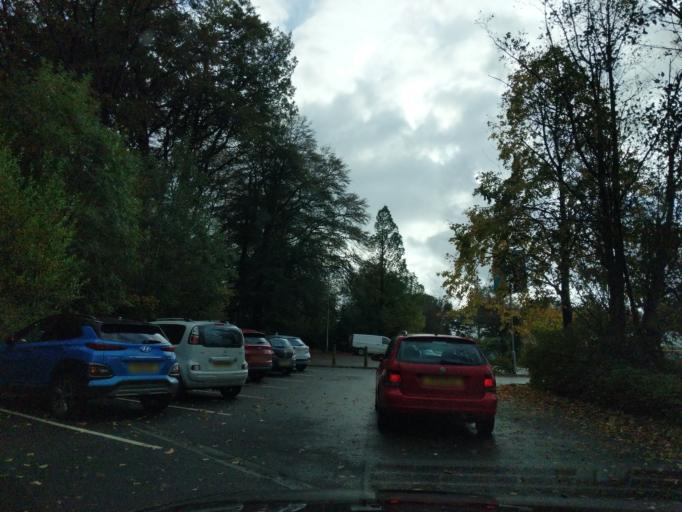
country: GB
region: Scotland
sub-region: Dumfries and Galloway
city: Castle Douglas
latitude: 54.9252
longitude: -3.9470
